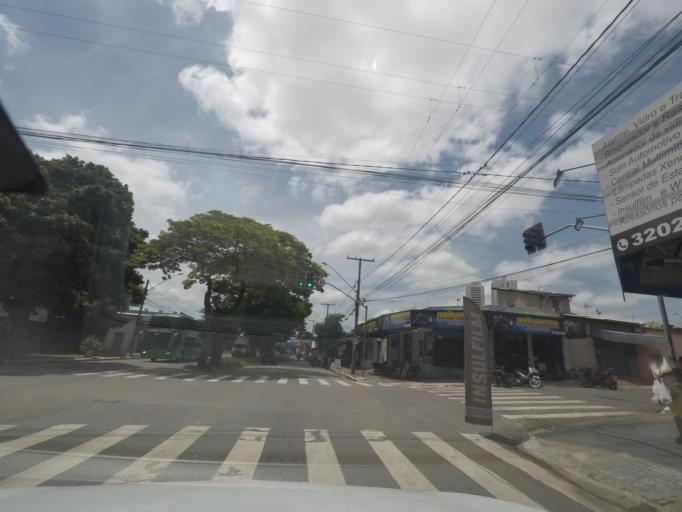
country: BR
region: Goias
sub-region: Goiania
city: Goiania
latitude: -16.6602
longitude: -49.2427
